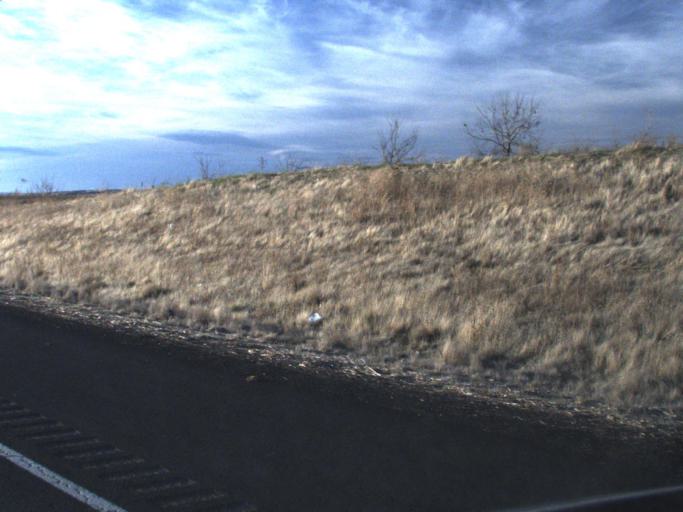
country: US
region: Washington
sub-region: Walla Walla County
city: Garrett
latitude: 46.0723
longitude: -118.3996
